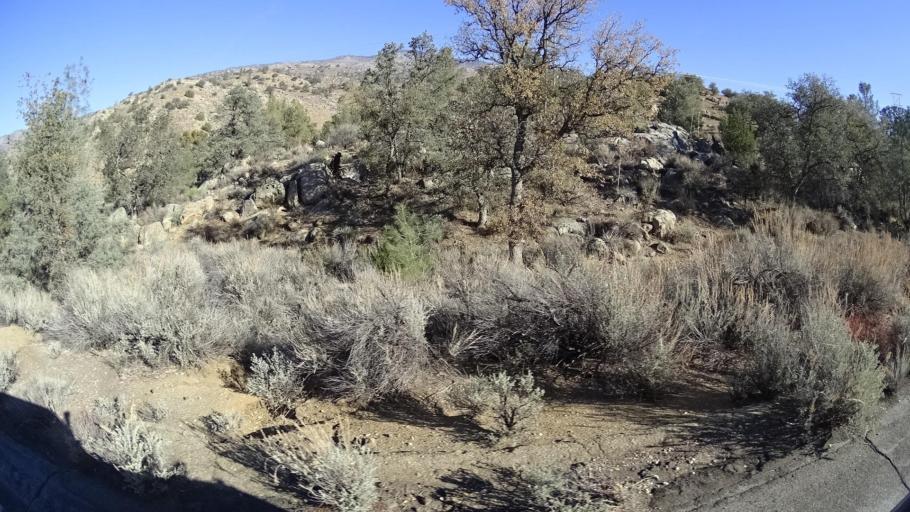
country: US
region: California
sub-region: Kern County
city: Bodfish
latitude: 35.3850
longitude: -118.4211
